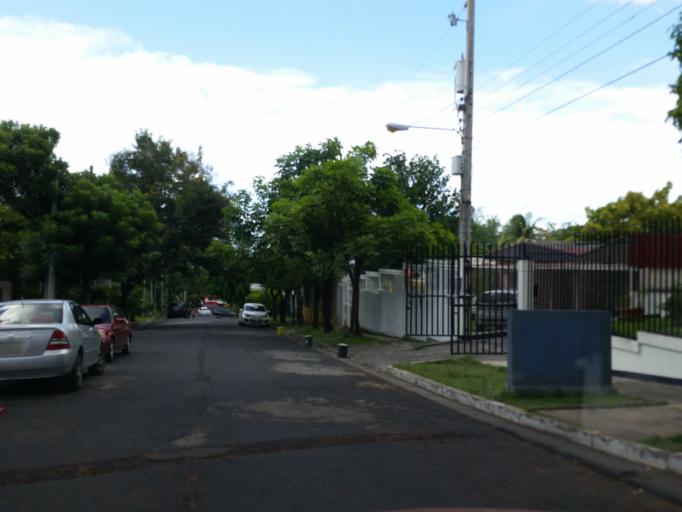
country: NI
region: Managua
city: Managua
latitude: 12.1012
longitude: -86.2661
